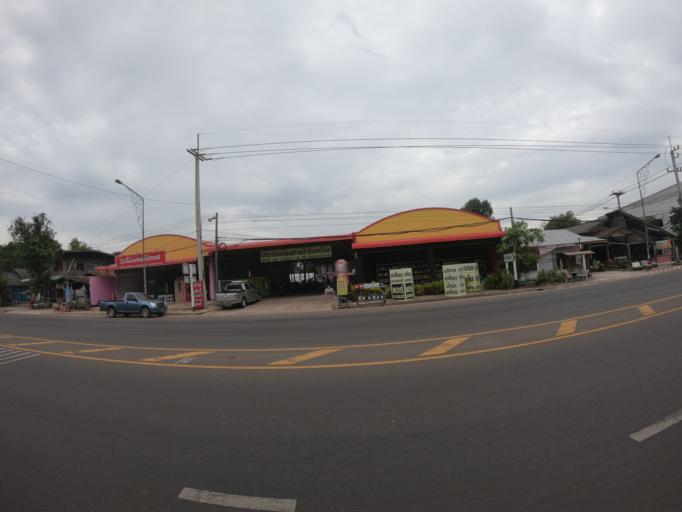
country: TH
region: Roi Et
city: Chiang Khwan
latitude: 16.1108
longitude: 103.8447
